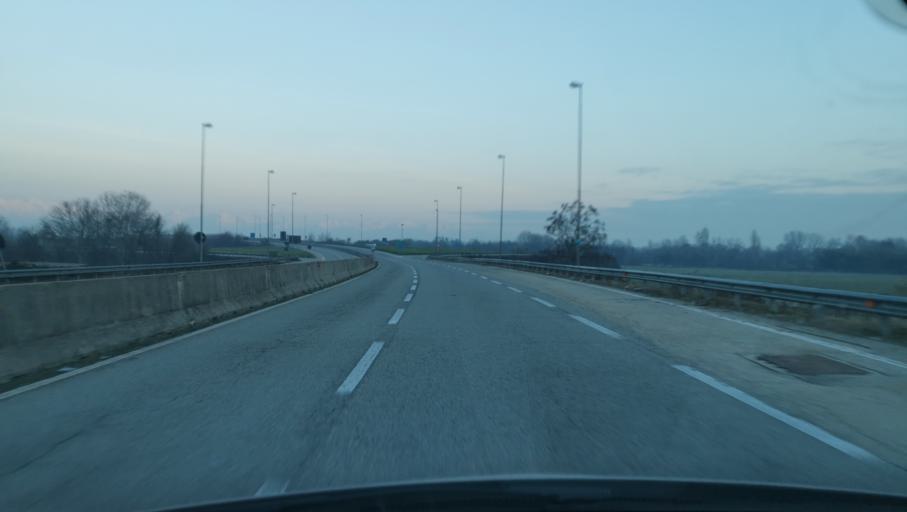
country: IT
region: Piedmont
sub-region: Provincia di Torino
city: Brandizzo
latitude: 45.1836
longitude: 7.8595
